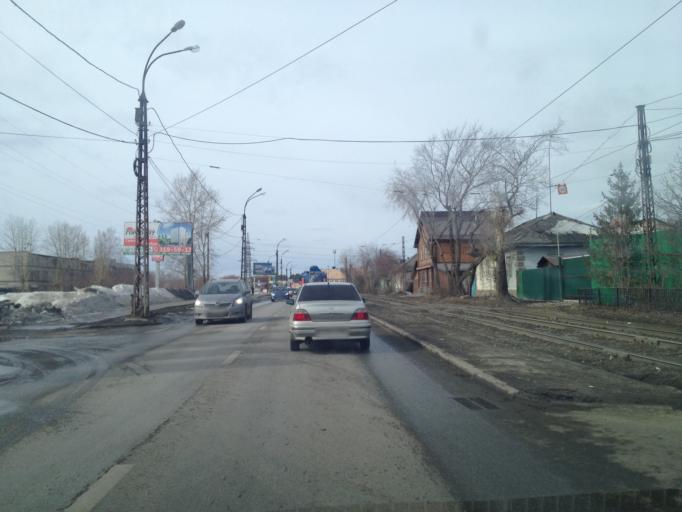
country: RU
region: Sverdlovsk
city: Sovkhoznyy
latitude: 56.7570
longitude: 60.5930
